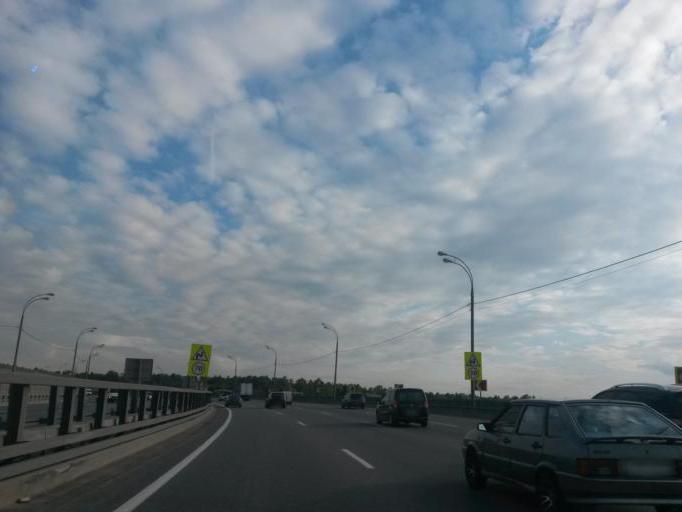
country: RU
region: Moskovskaya
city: Vidnoye
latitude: 55.5546
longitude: 37.6831
